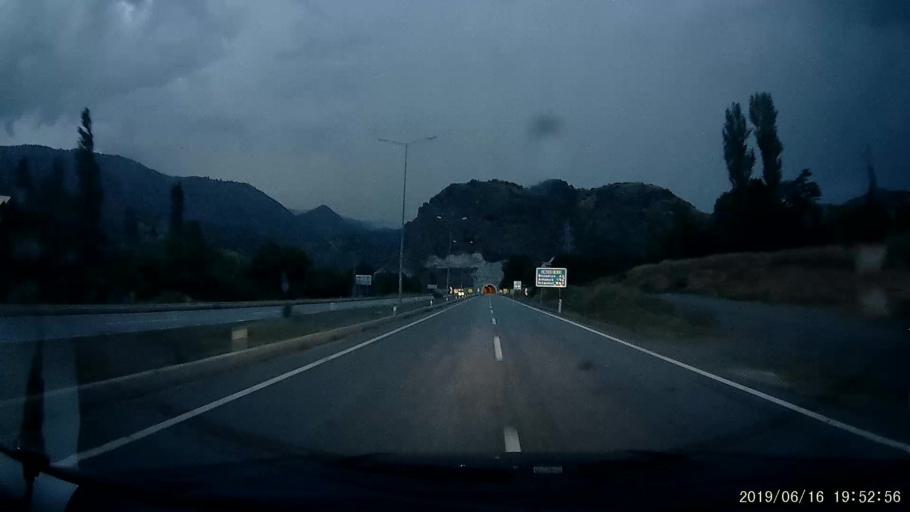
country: TR
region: Sivas
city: Koyulhisar
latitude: 40.2889
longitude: 37.7944
